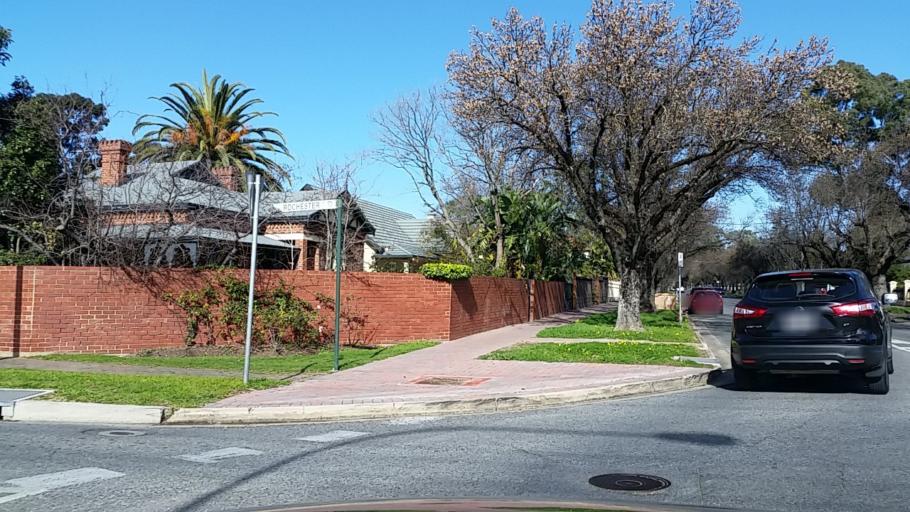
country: AU
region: South Australia
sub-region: Burnside
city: Tusmore
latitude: -34.9317
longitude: 138.6515
